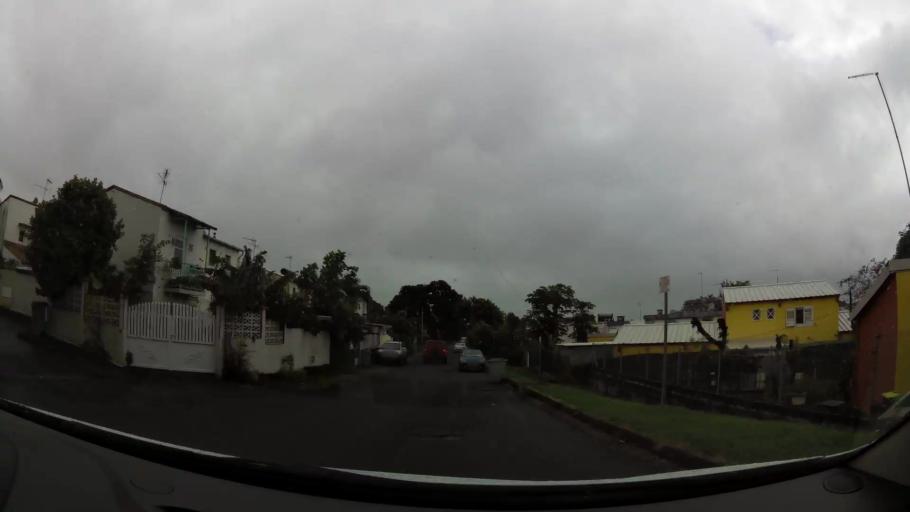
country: RE
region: Reunion
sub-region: Reunion
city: Saint-Andre
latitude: -20.9589
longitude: 55.6460
